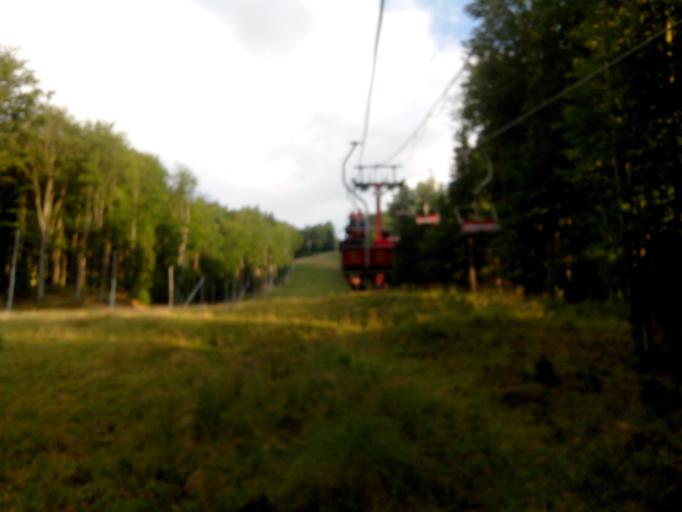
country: RO
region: Maramures
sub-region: Comuna Sisesti
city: Surdesti
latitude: 47.6730
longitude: 23.7815
